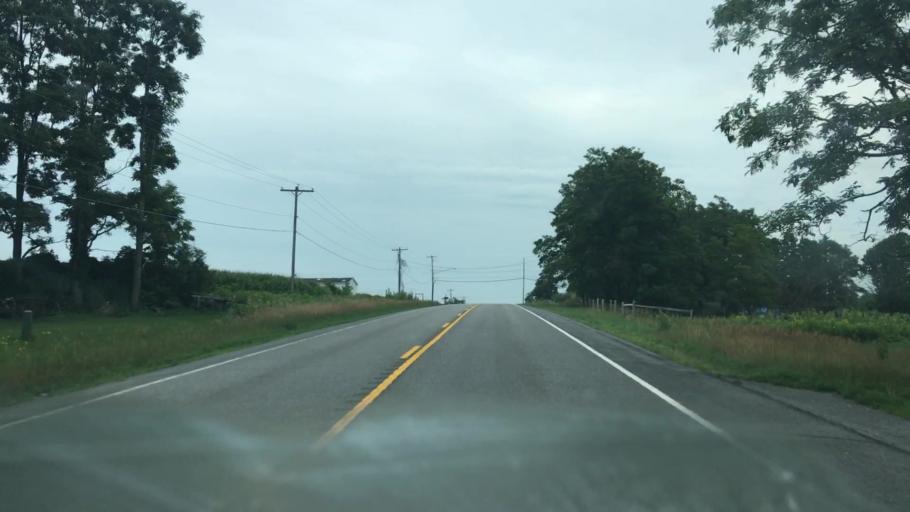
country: US
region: New York
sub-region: Clinton County
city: Morrisonville
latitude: 44.6444
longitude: -73.5665
